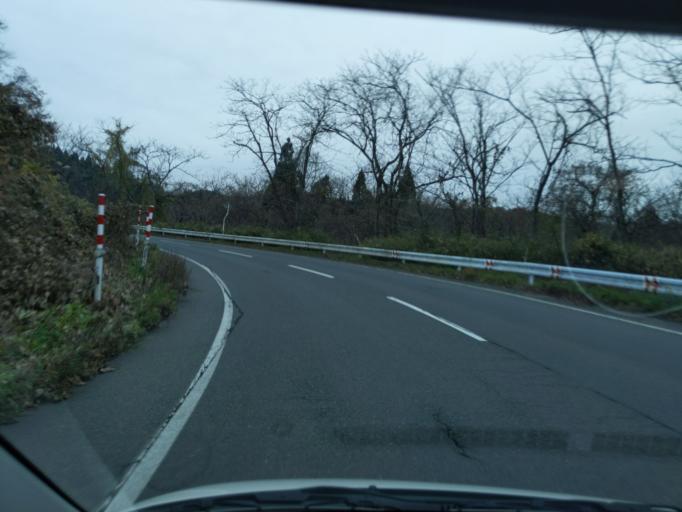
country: JP
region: Iwate
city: Kitakami
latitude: 39.2257
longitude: 141.2793
